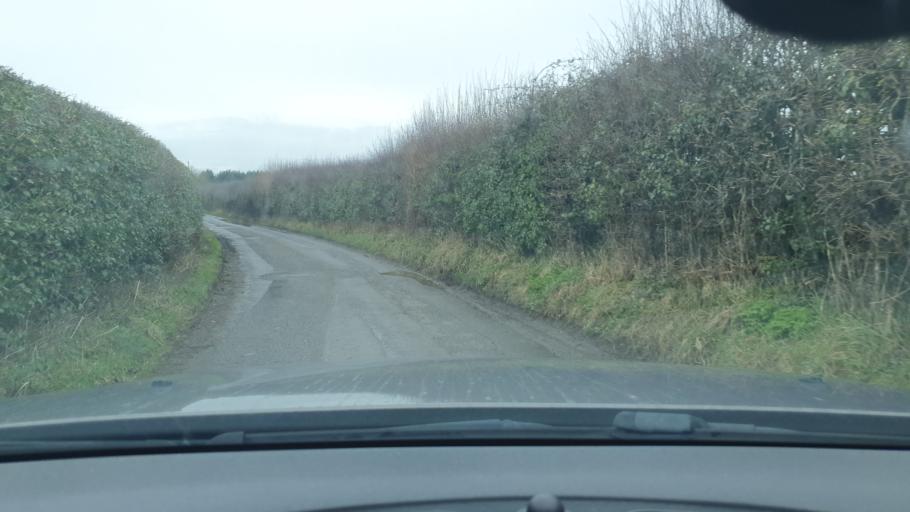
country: GB
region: England
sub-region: West Berkshire
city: Kintbury
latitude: 51.3984
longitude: -1.4369
